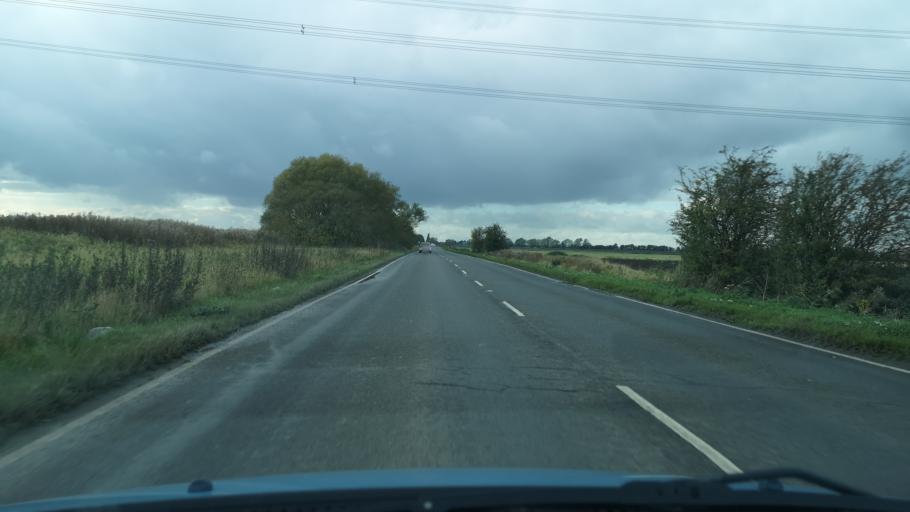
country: GB
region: England
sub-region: North Lincolnshire
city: Gunness
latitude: 53.5773
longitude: -0.7607
